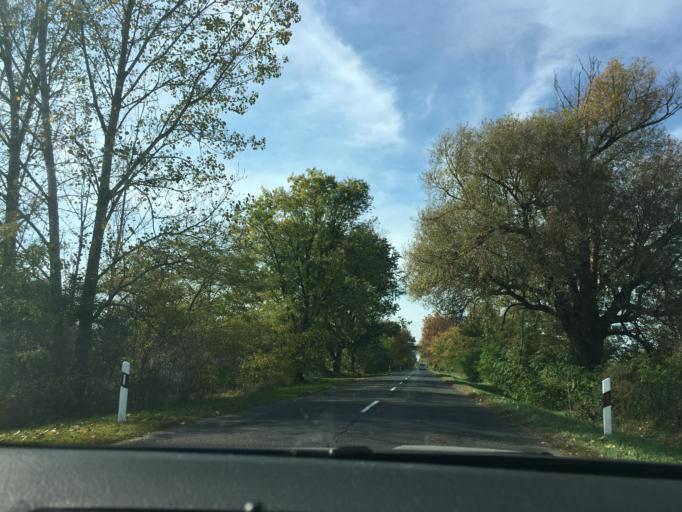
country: HU
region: Hajdu-Bihar
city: Nyirabrany
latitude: 47.5259
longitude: 21.9797
